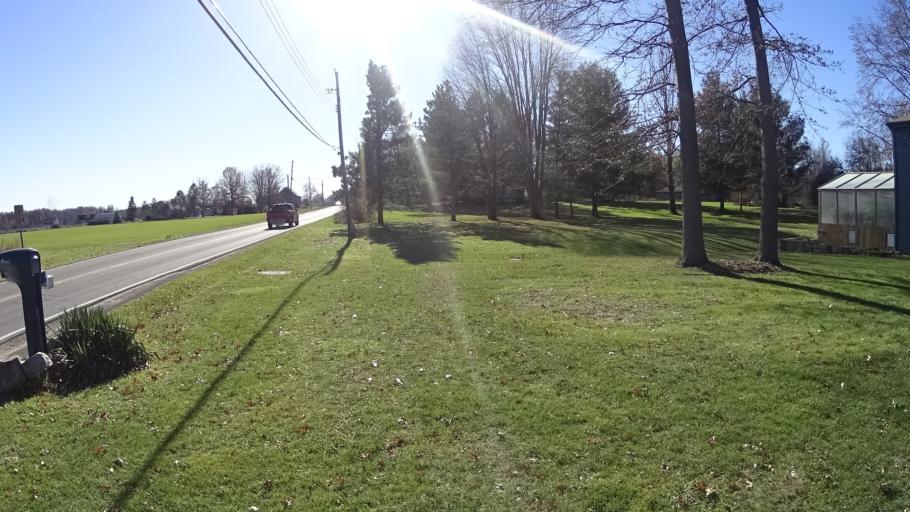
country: US
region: Ohio
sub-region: Lorain County
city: Elyria
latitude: 41.3360
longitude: -82.1516
